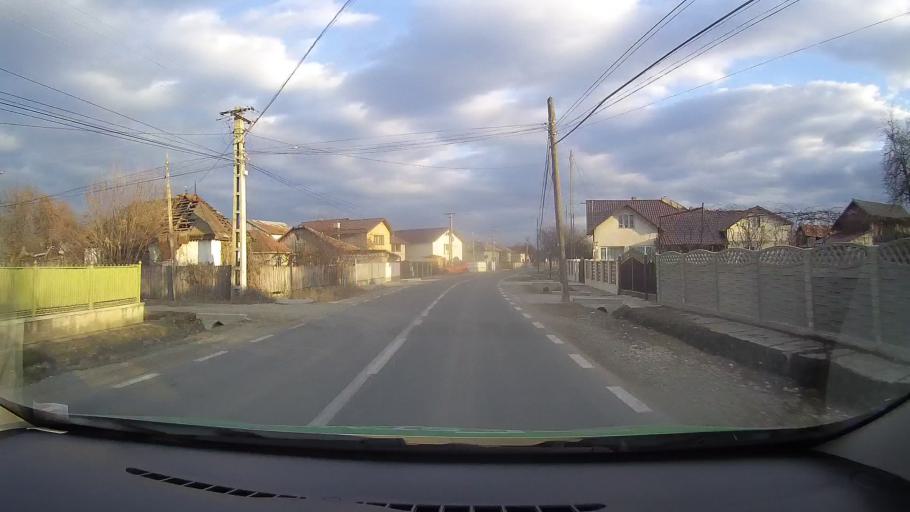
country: RO
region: Dambovita
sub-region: Comuna I. L. Caragiale
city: Ghirdoveni
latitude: 44.9405
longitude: 25.6717
